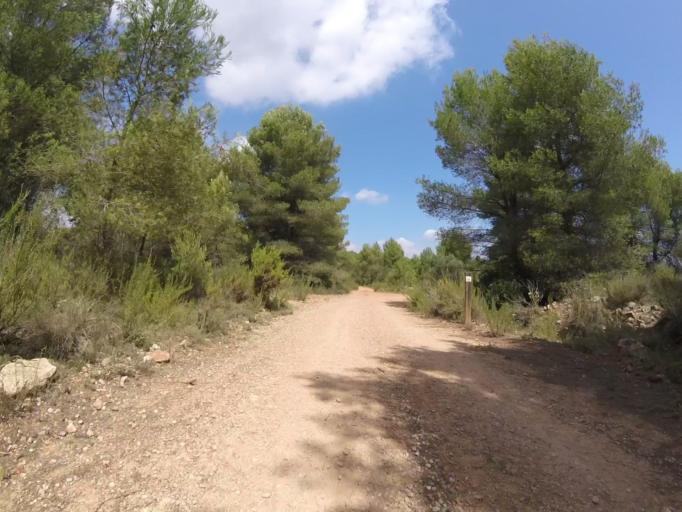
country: ES
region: Valencia
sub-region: Provincia de Castello
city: Torreblanca
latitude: 40.2058
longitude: 0.1370
